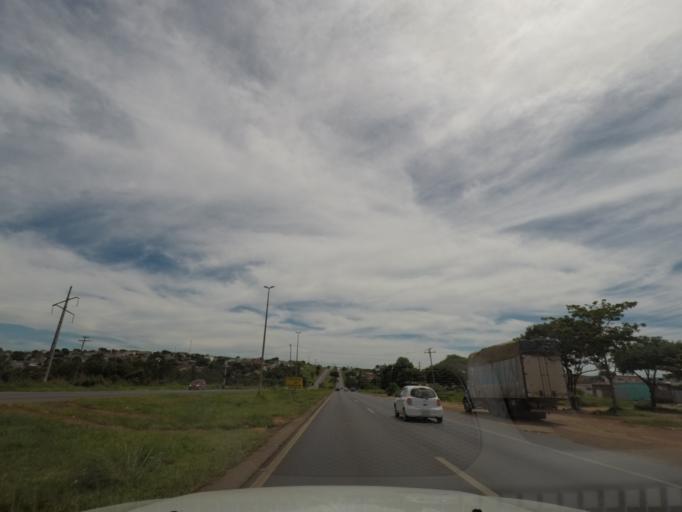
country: BR
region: Goias
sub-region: Planaltina
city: Planaltina
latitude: -15.6087
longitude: -47.6940
